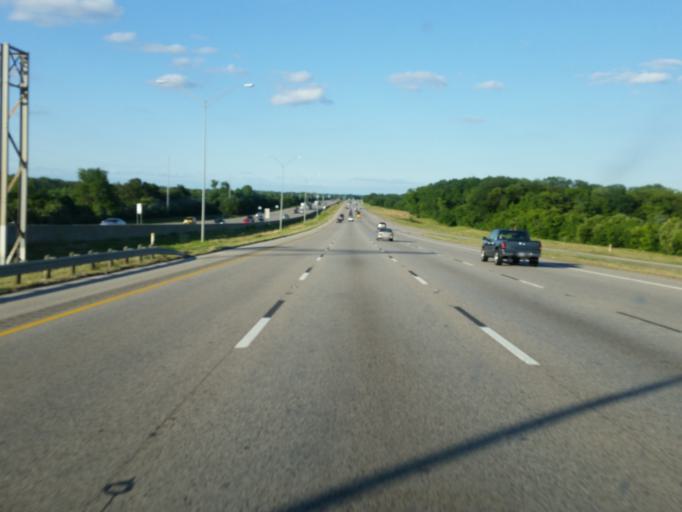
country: US
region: Texas
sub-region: Dallas County
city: Hutchins
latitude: 32.6655
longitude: -96.7188
